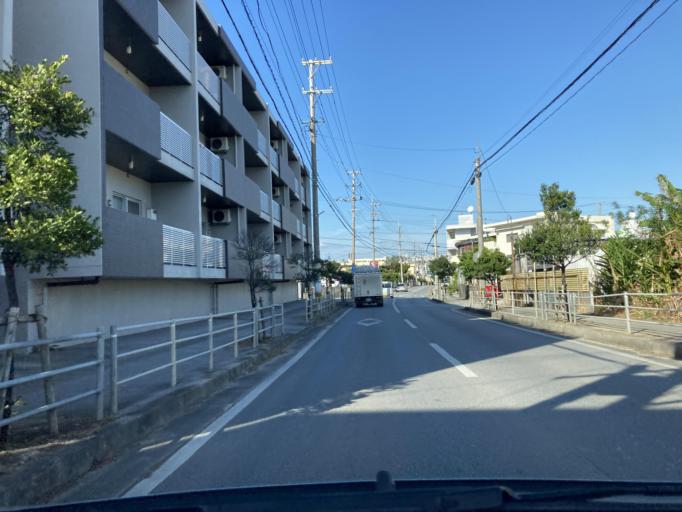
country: JP
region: Okinawa
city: Tomigusuku
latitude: 26.1823
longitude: 127.7068
